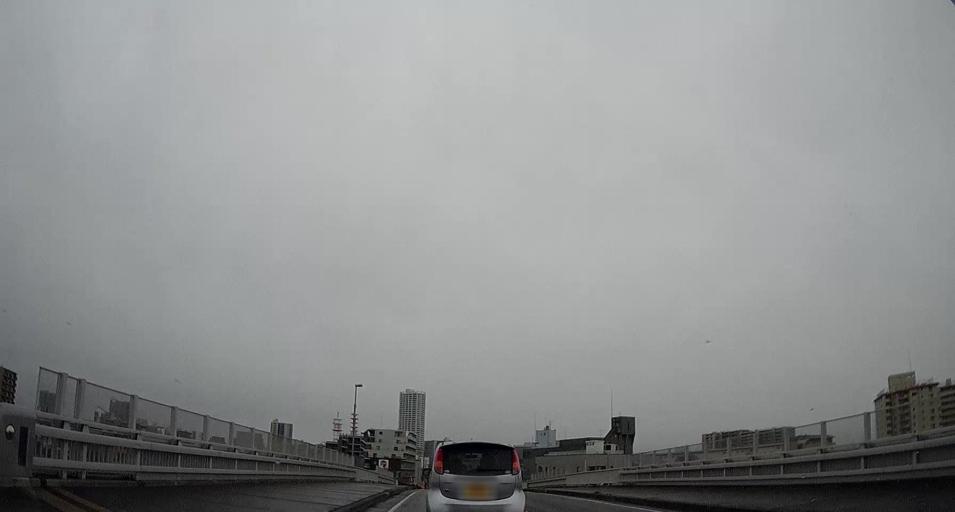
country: JP
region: Chiba
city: Funabashi
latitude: 35.7021
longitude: 139.9746
